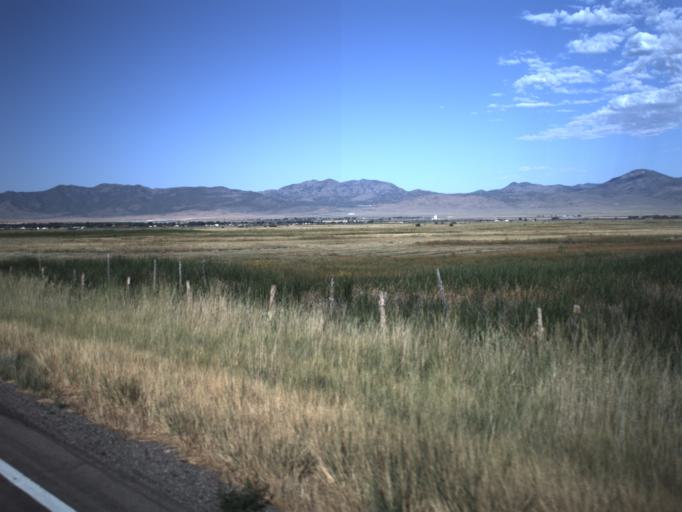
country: US
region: Utah
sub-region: Utah County
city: Genola
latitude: 39.9675
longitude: -111.8569
